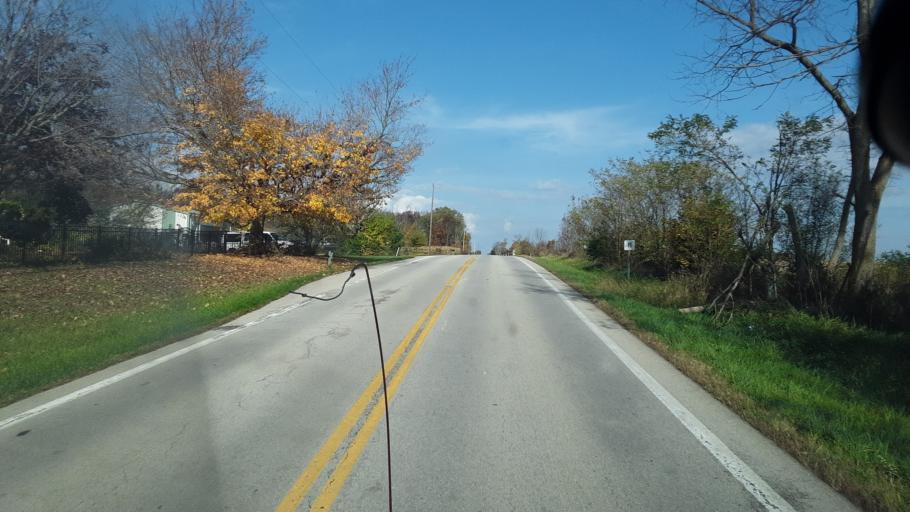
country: US
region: Ohio
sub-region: Clinton County
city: Sabina
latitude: 39.5140
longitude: -83.6910
